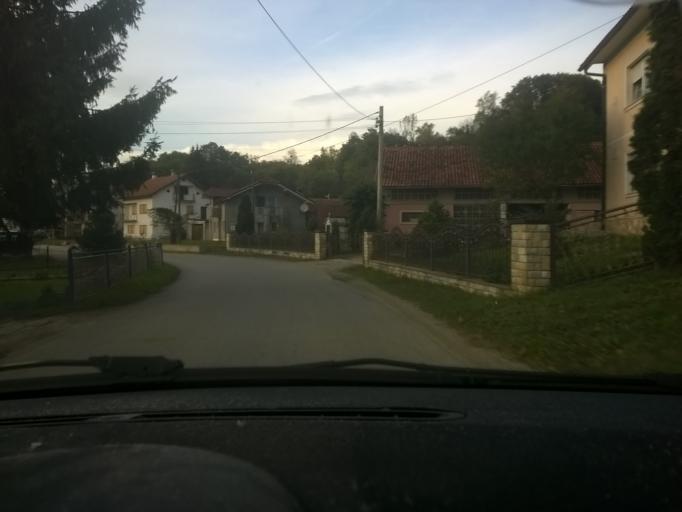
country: HR
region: Krapinsko-Zagorska
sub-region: Grad Krapina
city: Krapina
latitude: 46.0961
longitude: 15.8804
